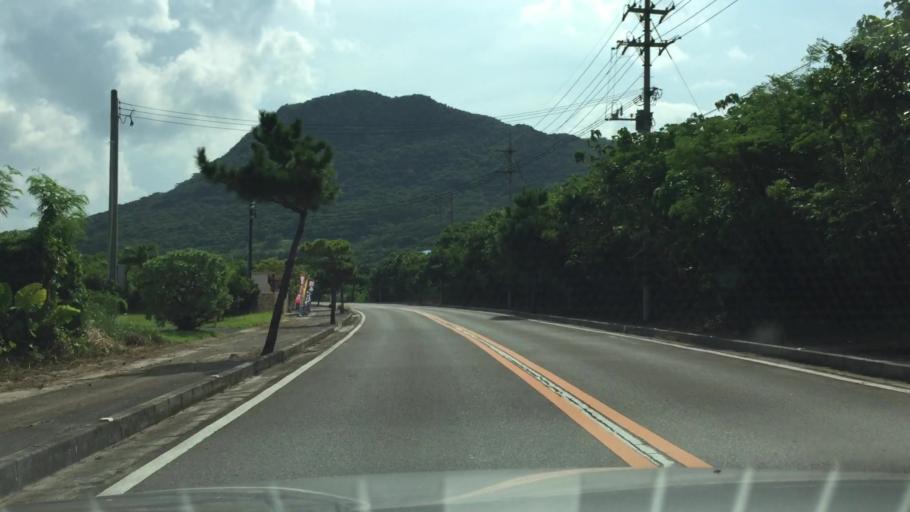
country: JP
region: Okinawa
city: Ishigaki
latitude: 24.4889
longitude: 124.2759
